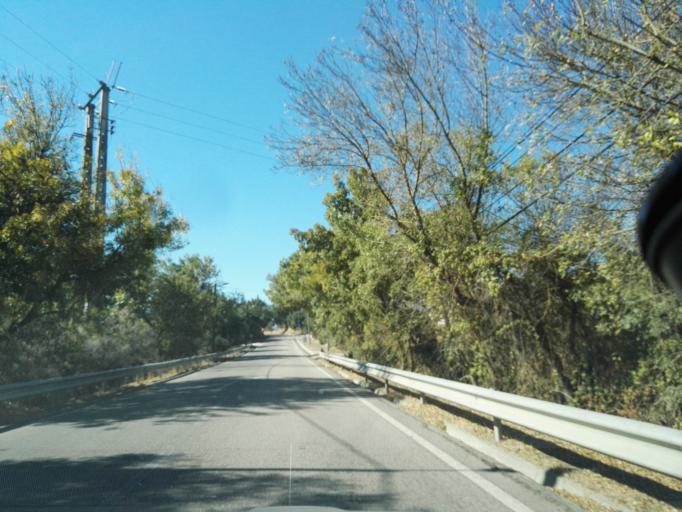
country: PT
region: Santarem
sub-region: Benavente
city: Poceirao
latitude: 38.8562
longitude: -8.7317
